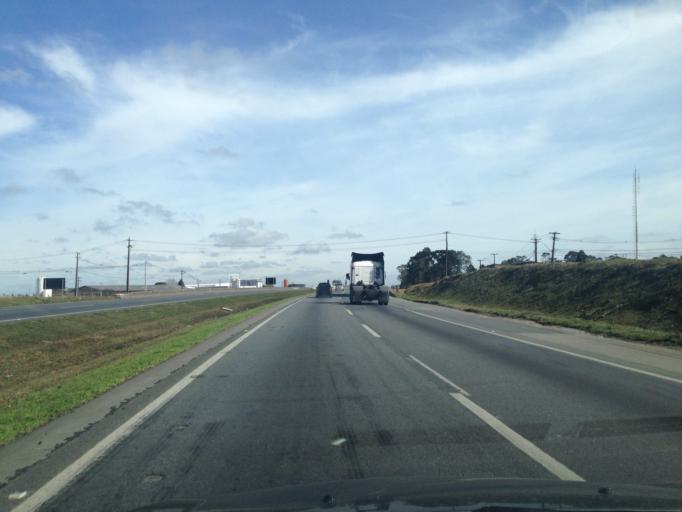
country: BR
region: Parana
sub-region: Sao Jose Dos Pinhais
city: Sao Jose dos Pinhais
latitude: -25.5644
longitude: -49.1574
